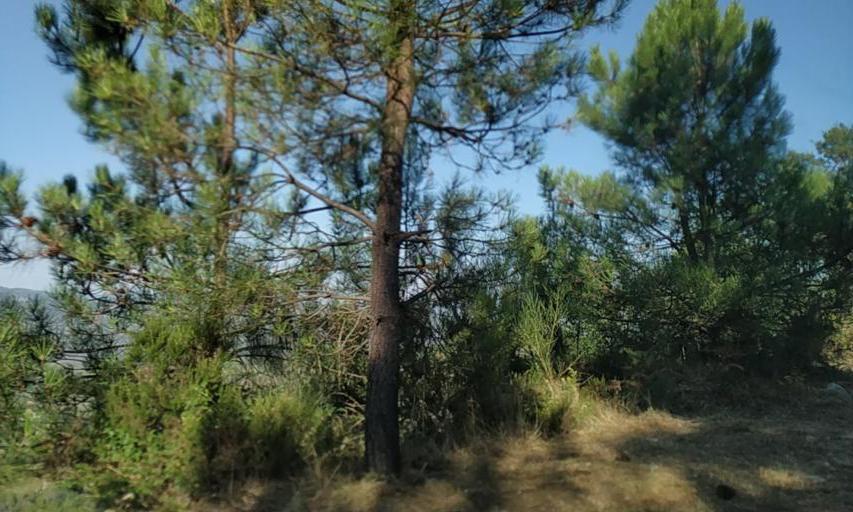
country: PT
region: Viseu
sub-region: Sao Joao da Pesqueira
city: Sao Joao da Pesqueira
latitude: 41.1648
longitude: -7.4337
